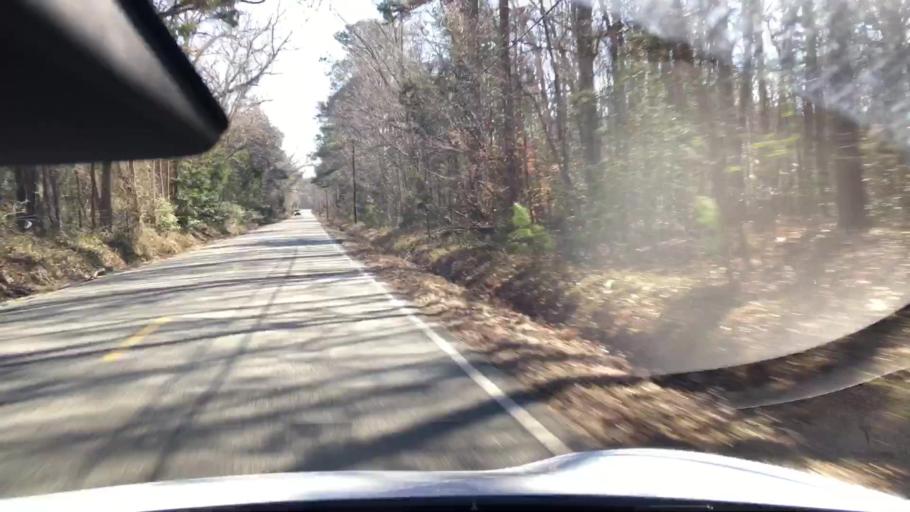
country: US
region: Virginia
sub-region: Henrico County
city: Short Pump
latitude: 37.5824
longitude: -77.7434
